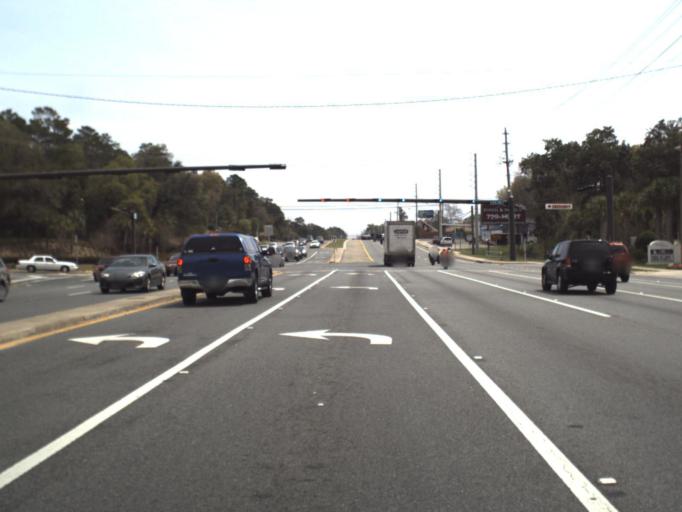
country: US
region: Florida
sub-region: Okaloosa County
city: Niceville
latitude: 30.5224
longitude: -86.4946
